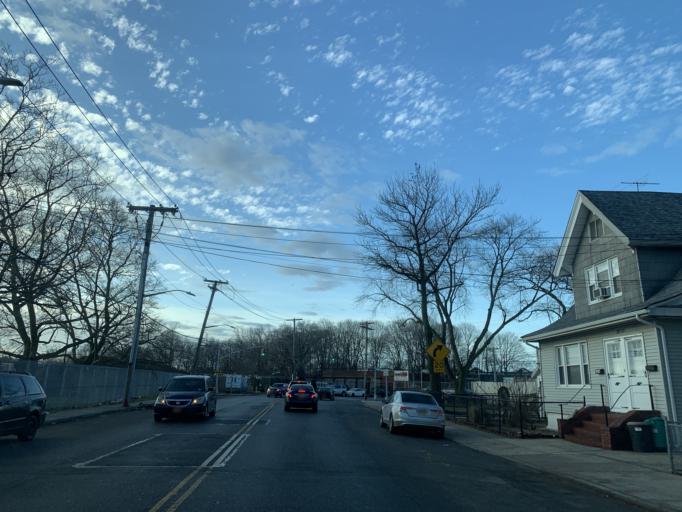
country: US
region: New York
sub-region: Queens County
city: Borough of Queens
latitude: 40.6756
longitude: -73.8360
